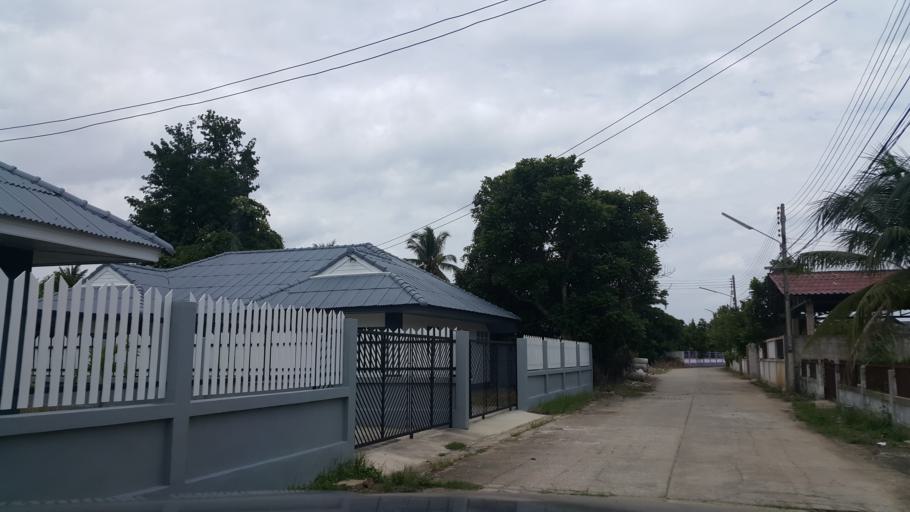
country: TH
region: Chiang Mai
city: Saraphi
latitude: 18.7073
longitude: 98.9798
